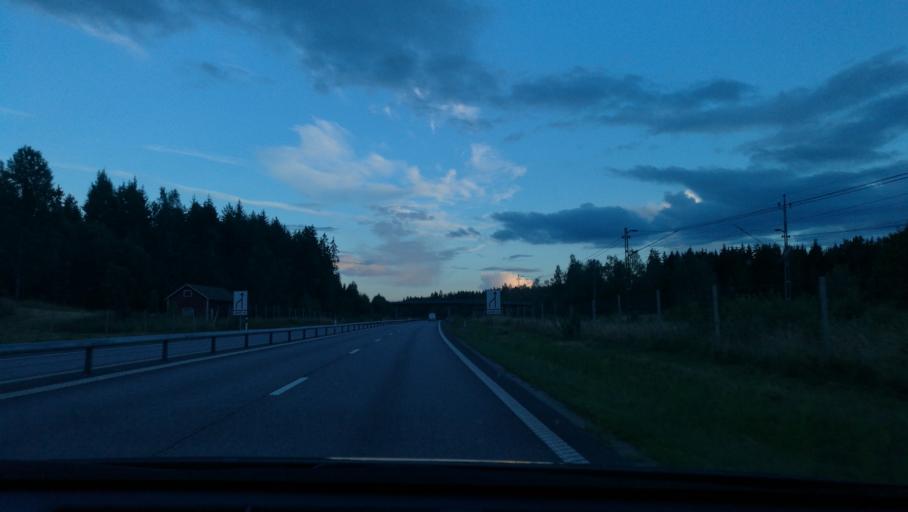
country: SE
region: Soedermanland
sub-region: Katrineholms Kommun
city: Katrineholm
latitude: 58.9276
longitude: 16.1960
